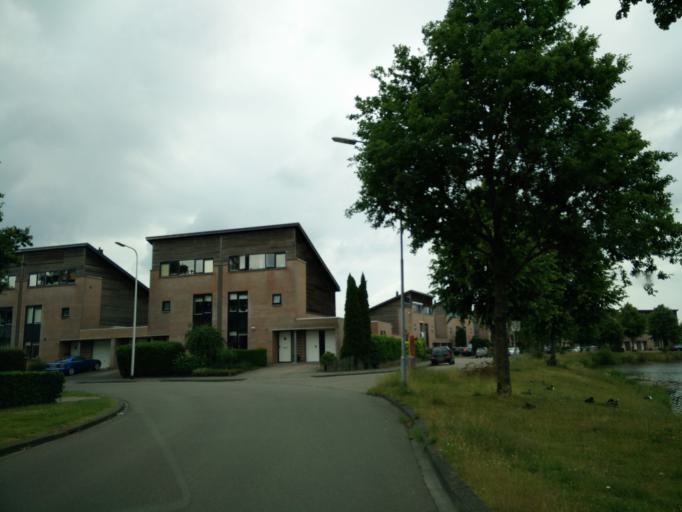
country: NL
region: Drenthe
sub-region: Gemeente Assen
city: Assen
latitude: 53.0241
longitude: 6.5946
